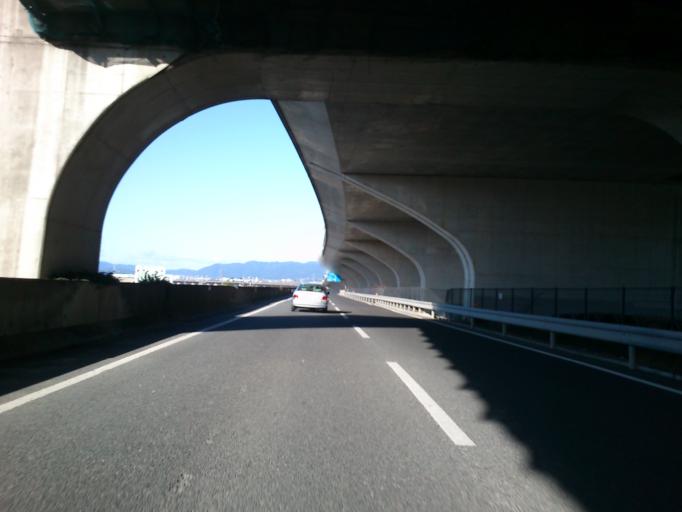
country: JP
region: Kyoto
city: Yawata
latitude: 34.8471
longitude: 135.7263
